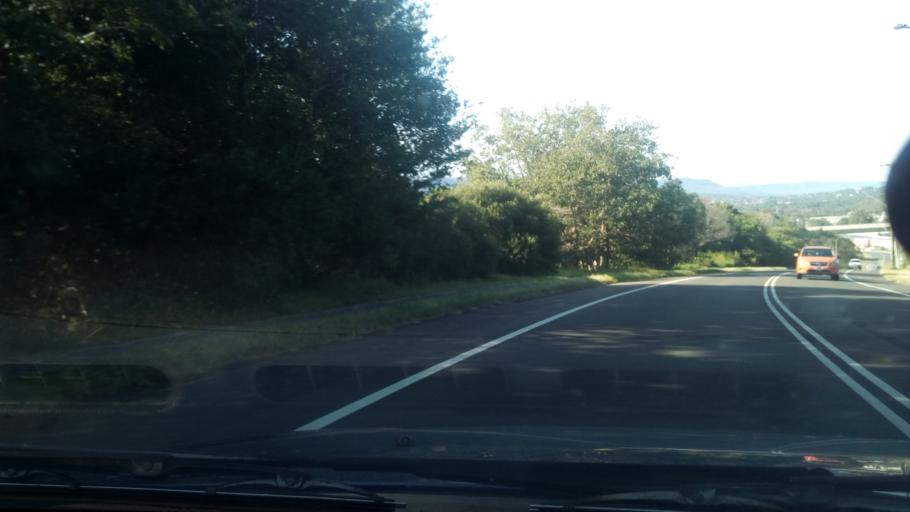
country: AU
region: New South Wales
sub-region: Wollongong
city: Berkeley
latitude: -34.4685
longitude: 150.8523
